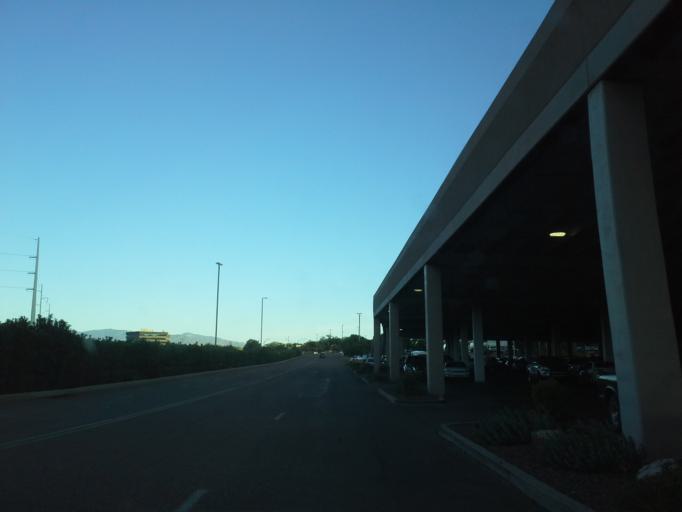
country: US
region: Arizona
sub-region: Pima County
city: Flowing Wells
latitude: 32.2911
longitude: -110.9740
